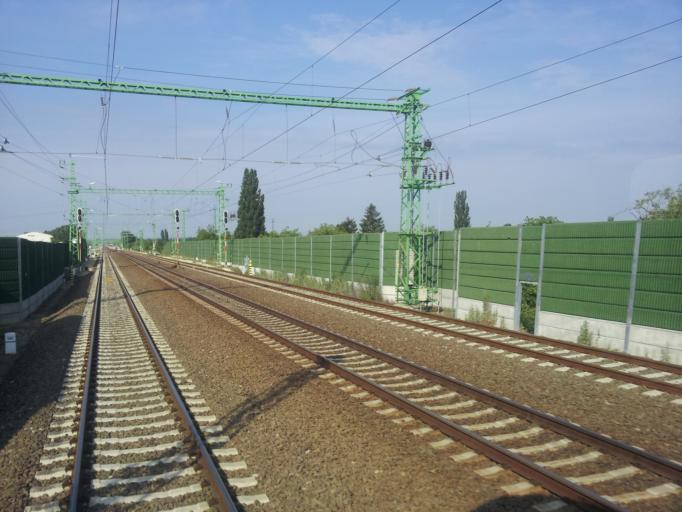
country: HU
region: Pest
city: Erd
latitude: 47.3710
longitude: 18.8859
